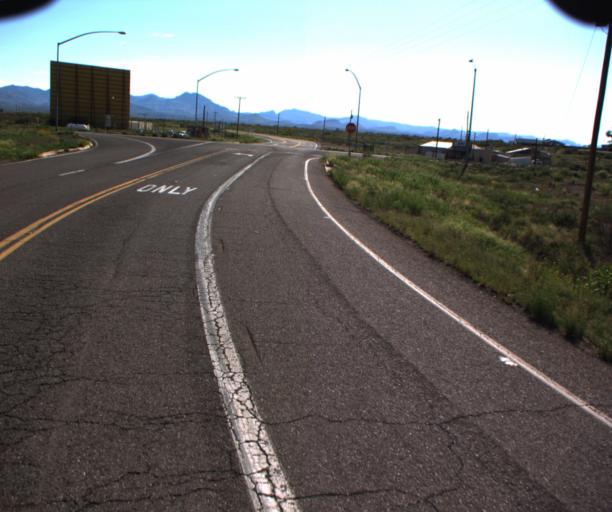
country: US
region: Arizona
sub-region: Greenlee County
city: Clifton
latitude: 32.9481
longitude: -109.2307
